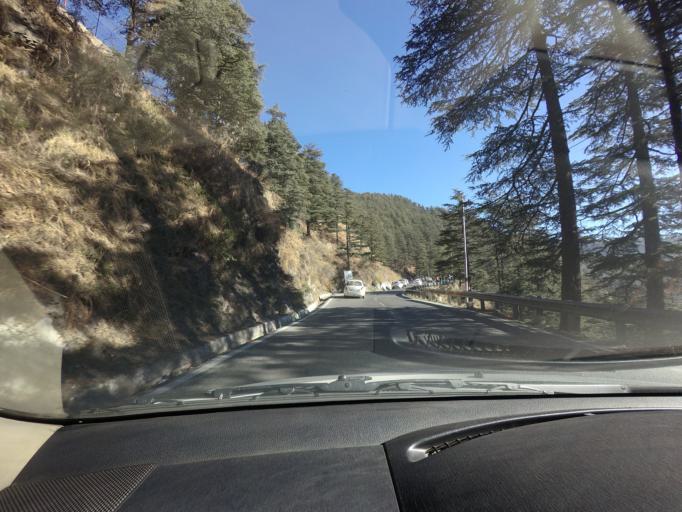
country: IN
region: Himachal Pradesh
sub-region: Shimla
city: Shimla
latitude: 31.1143
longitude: 77.2230
